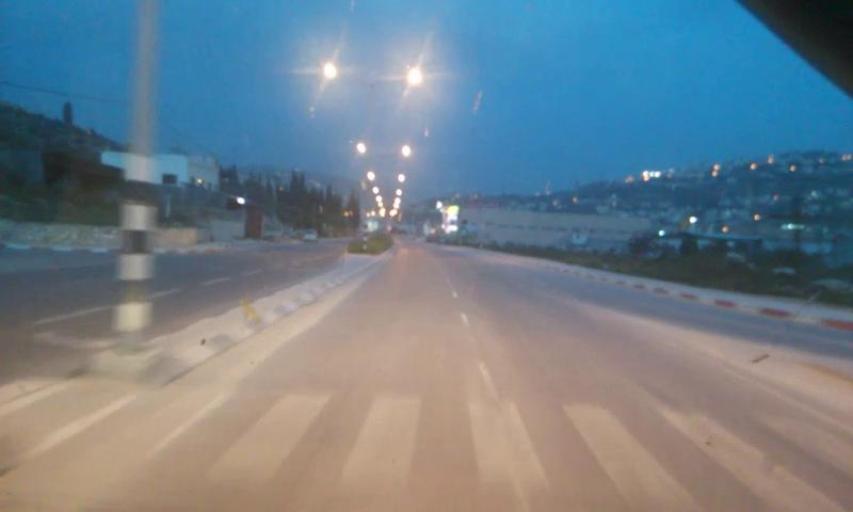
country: PS
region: West Bank
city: Bayt Iba
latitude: 32.2428
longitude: 35.1995
